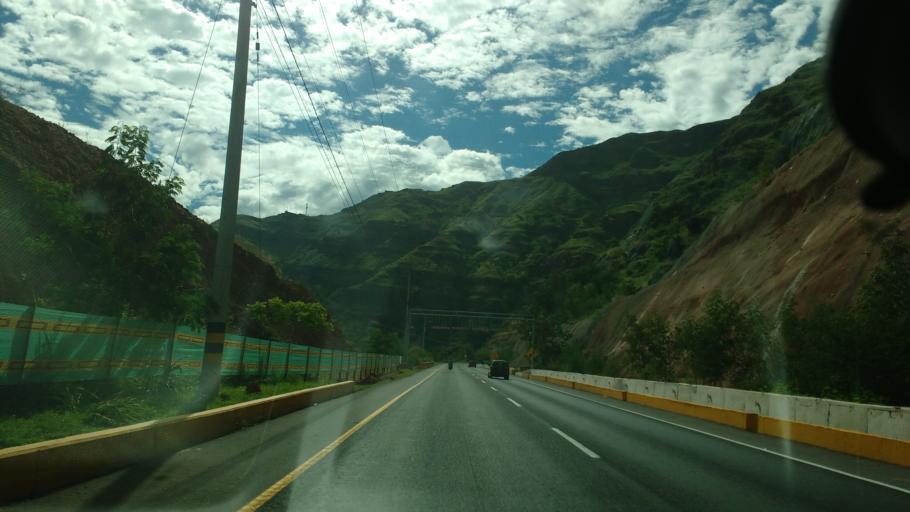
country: CO
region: Tolima
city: Valle de San Juan
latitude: 4.2830
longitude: -75.0200
